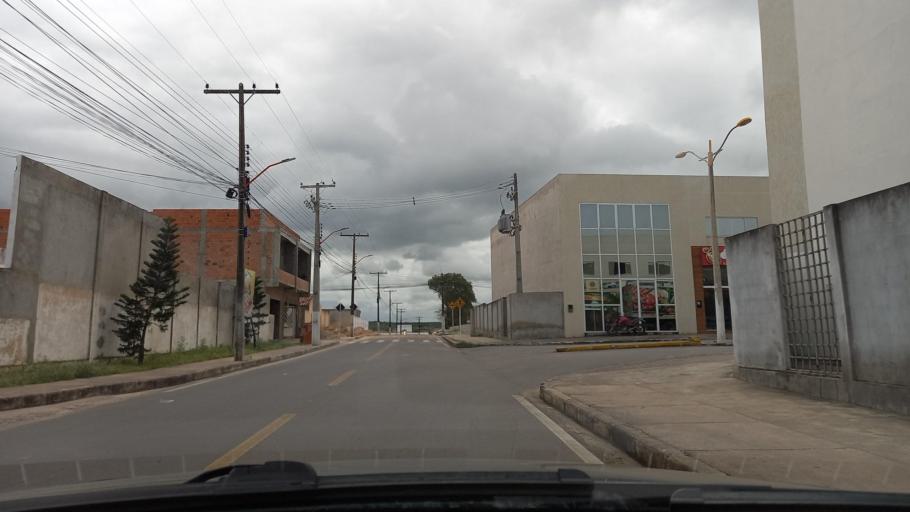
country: BR
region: Sergipe
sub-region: Caninde De Sao Francisco
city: Caninde de Sao Francisco
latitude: -9.6095
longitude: -37.7635
